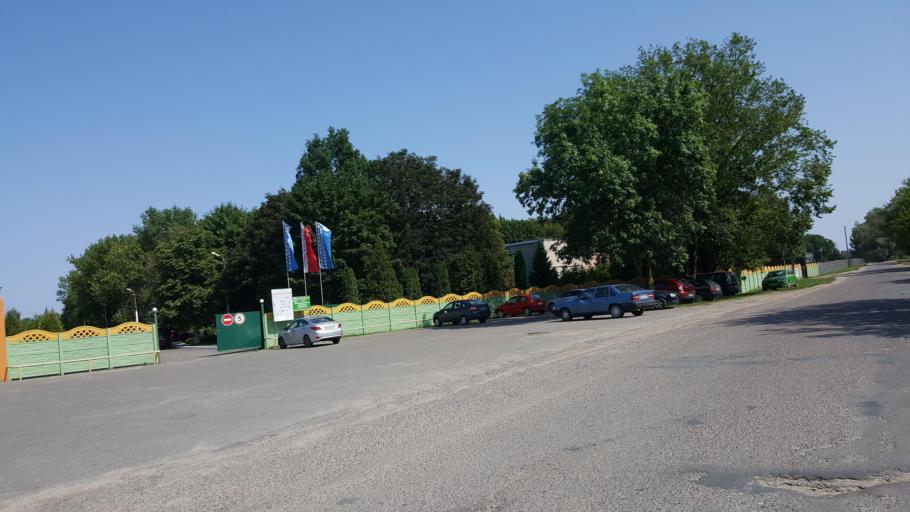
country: BY
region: Brest
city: Zhabinka
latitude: 52.2036
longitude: 24.0087
